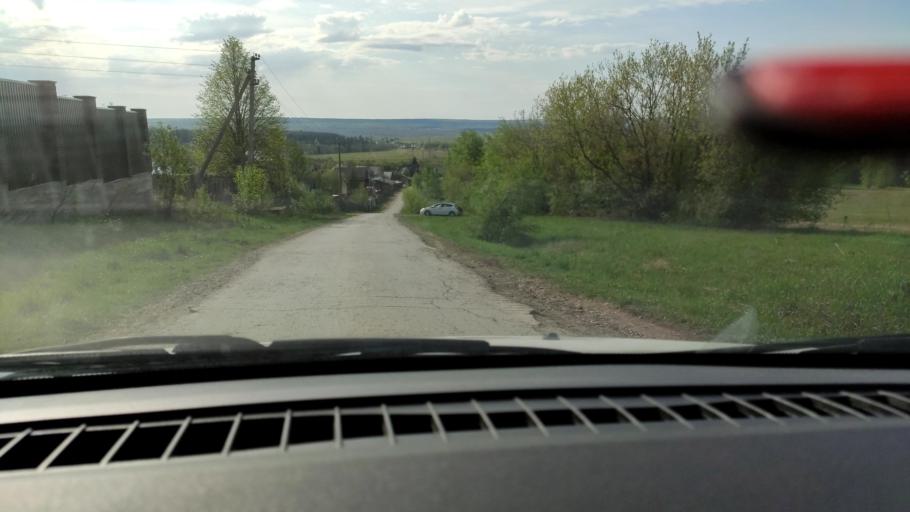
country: RU
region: Perm
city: Froly
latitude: 57.9480
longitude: 56.2966
